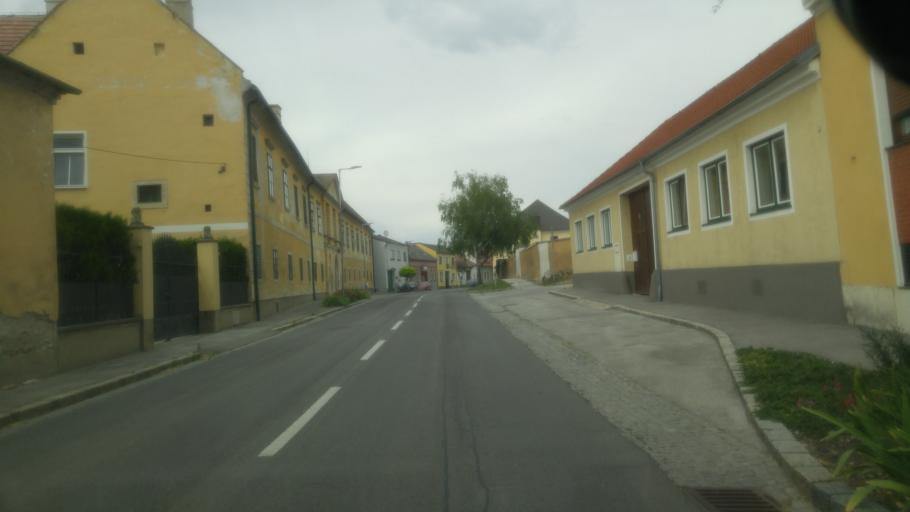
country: AT
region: Lower Austria
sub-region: Politischer Bezirk Wien-Umgebung
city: Moosbrunn
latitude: 48.0415
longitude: 16.4448
